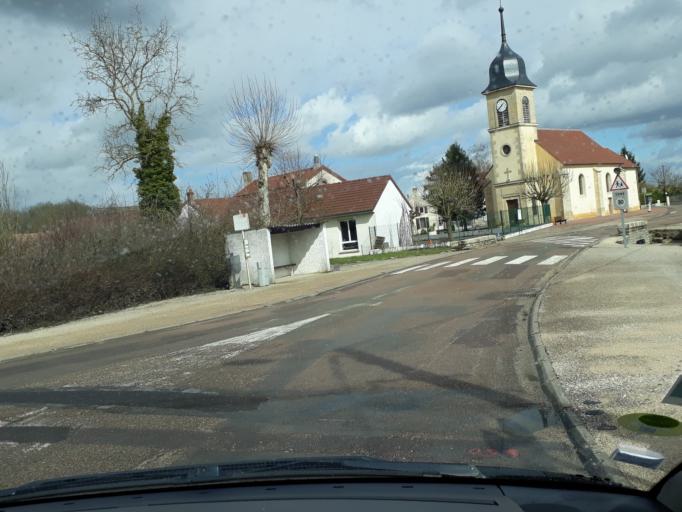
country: FR
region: Bourgogne
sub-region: Departement de la Cote-d'Or
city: Longecourt-en-Plaine
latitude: 47.2121
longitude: 5.1831
